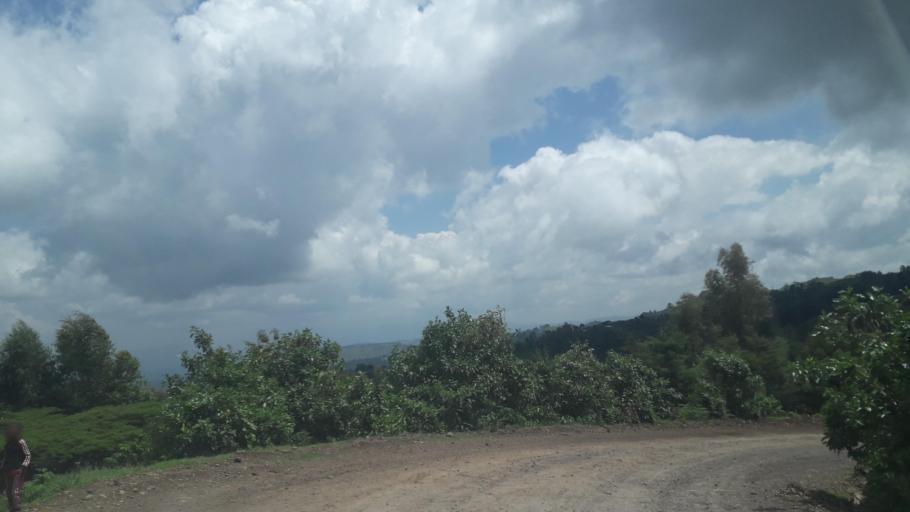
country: ET
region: Oromiya
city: Jima
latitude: 7.4586
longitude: 36.8719
